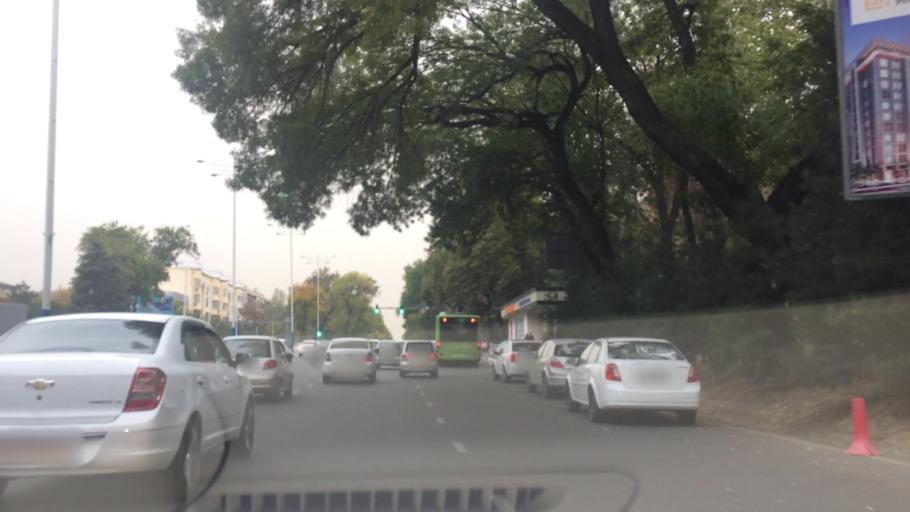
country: UZ
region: Toshkent Shahri
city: Tashkent
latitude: 41.3073
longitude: 69.2938
